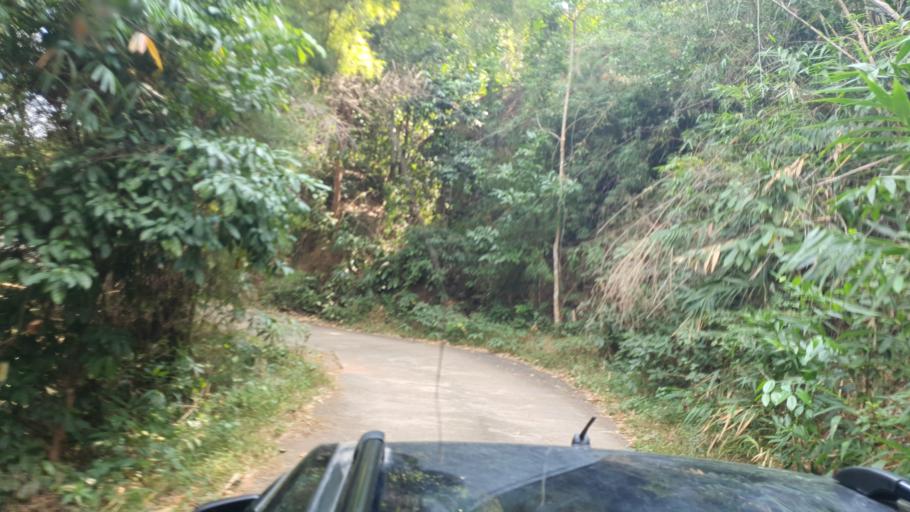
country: TH
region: Changwat Bueng Kan
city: Si Wilai
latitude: 18.2705
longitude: 103.7970
